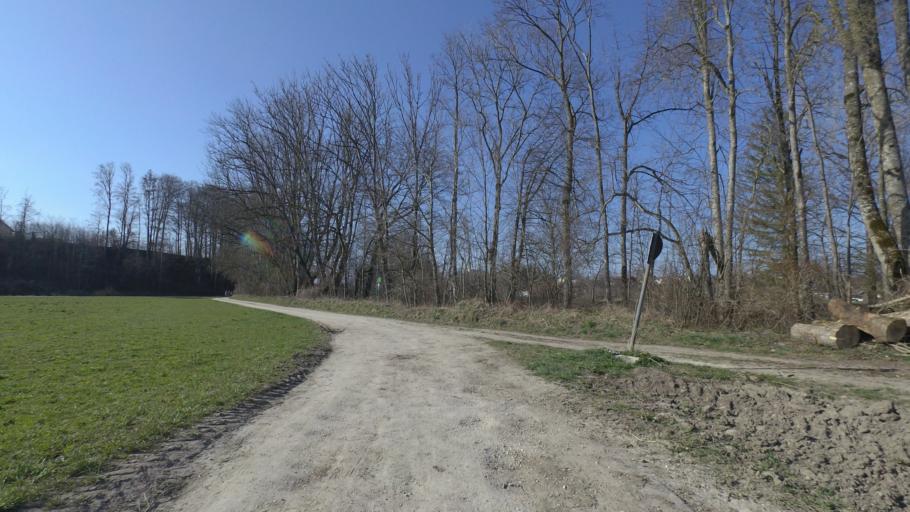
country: DE
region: Bavaria
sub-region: Upper Bavaria
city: Nussdorf
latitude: 47.9329
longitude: 12.6061
